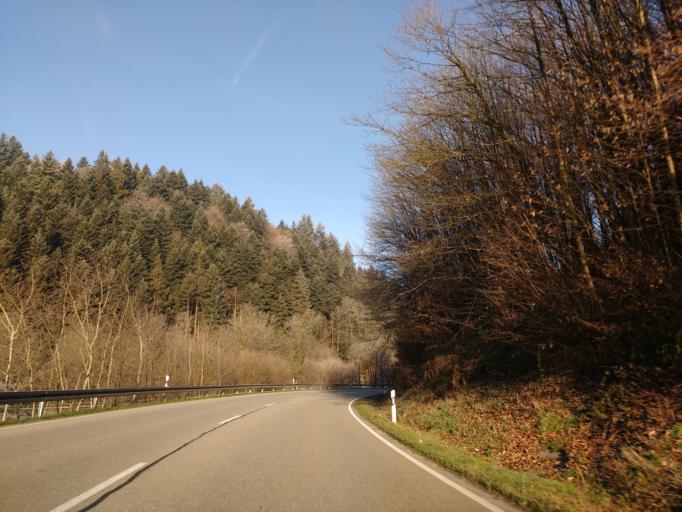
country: DE
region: Baden-Wuerttemberg
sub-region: Freiburg Region
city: Oppenau
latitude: 48.5029
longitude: 8.1364
